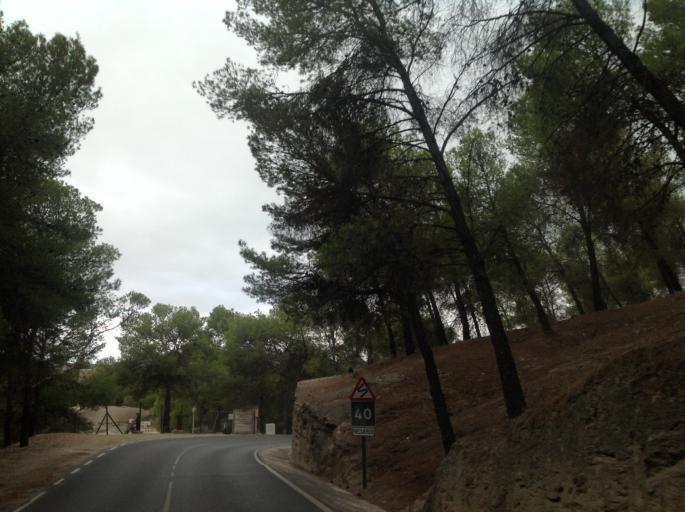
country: ES
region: Andalusia
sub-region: Provincia de Malaga
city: Ardales
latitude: 36.9202
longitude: -4.8027
